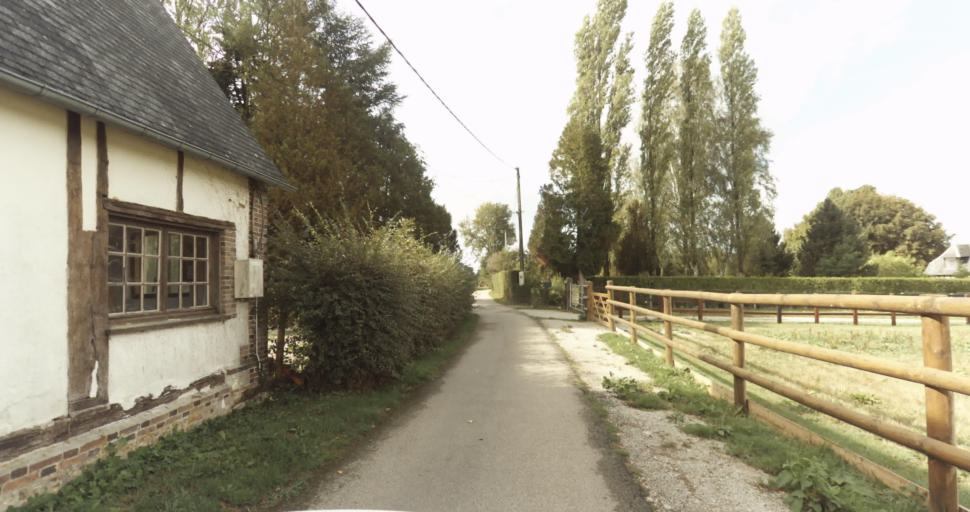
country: FR
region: Lower Normandy
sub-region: Departement de l'Orne
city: Gace
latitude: 48.8367
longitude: 0.3874
